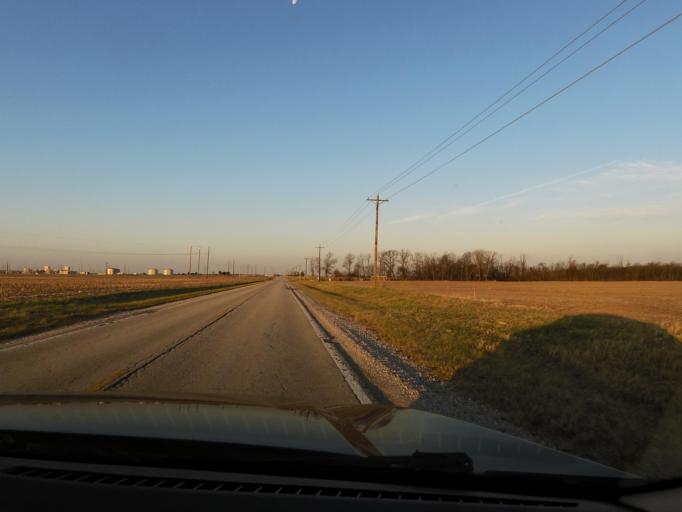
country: US
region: Illinois
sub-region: Marion County
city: Salem
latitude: 38.7652
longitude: -89.0016
